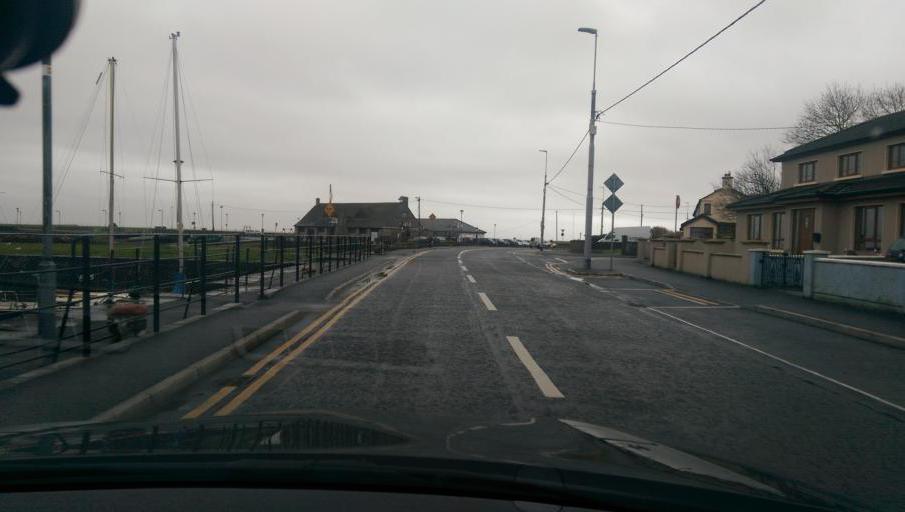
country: IE
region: Connaught
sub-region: County Galway
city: Gaillimh
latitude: 53.2682
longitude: -9.0550
